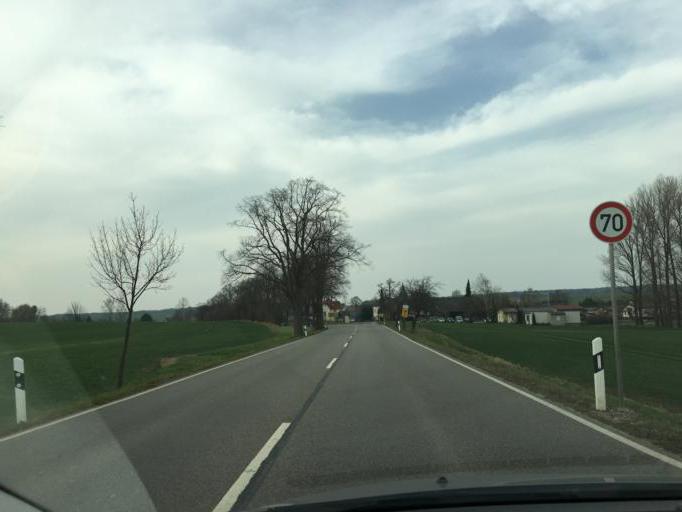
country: DE
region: Thuringia
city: Juckelberg
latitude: 50.9607
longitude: 12.6600
